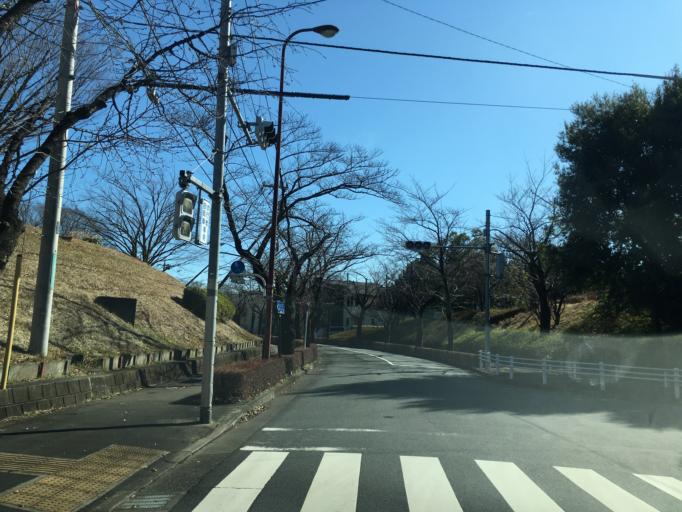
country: JP
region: Tokyo
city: Hino
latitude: 35.6213
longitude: 139.4462
